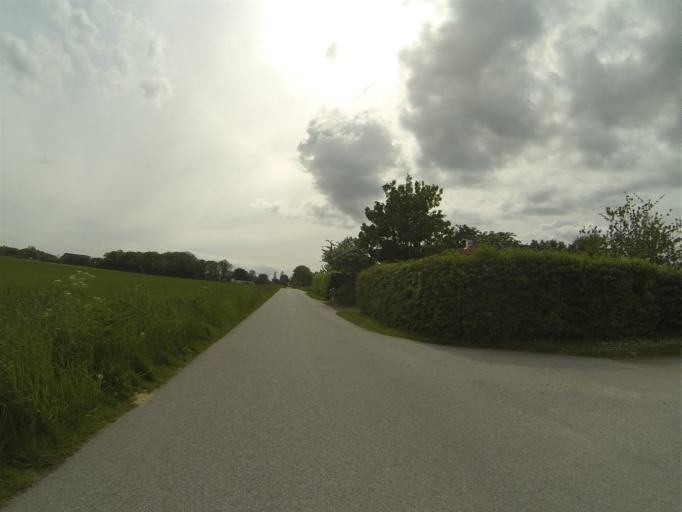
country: SE
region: Skane
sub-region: Lunds Kommun
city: Lund
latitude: 55.6981
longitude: 13.3011
